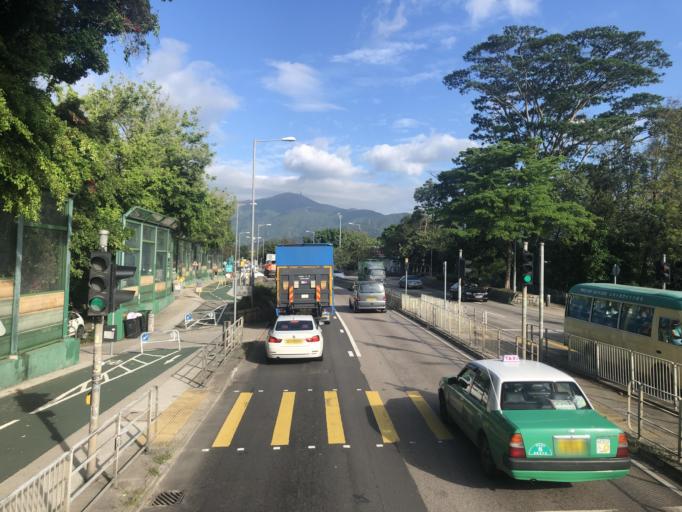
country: HK
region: Yuen Long
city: Yuen Long Kau Hui
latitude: 22.4406
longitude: 114.0557
